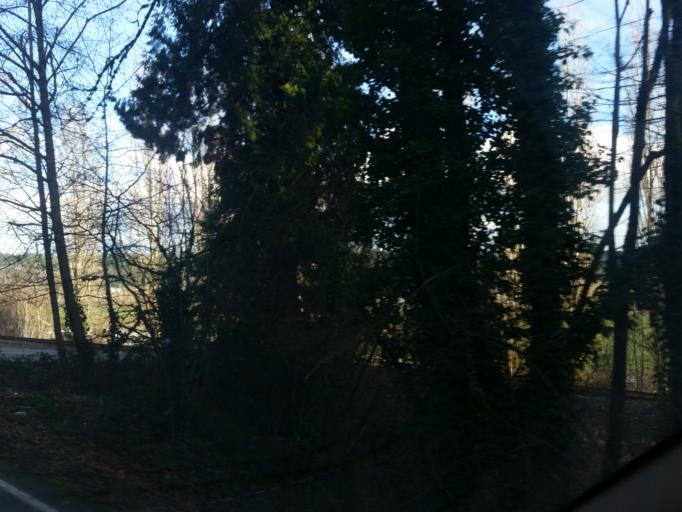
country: US
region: Washington
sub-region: King County
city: Kingsgate
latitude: 47.7162
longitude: -122.1545
